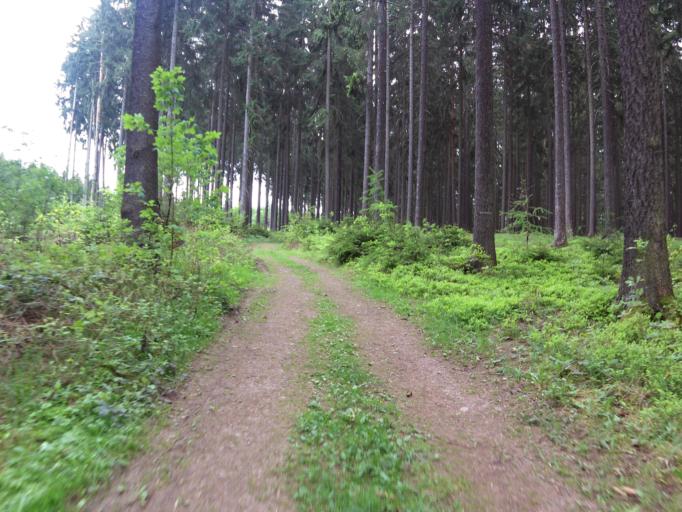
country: DE
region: Thuringia
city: Georgenthal
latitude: 50.8205
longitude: 10.6641
